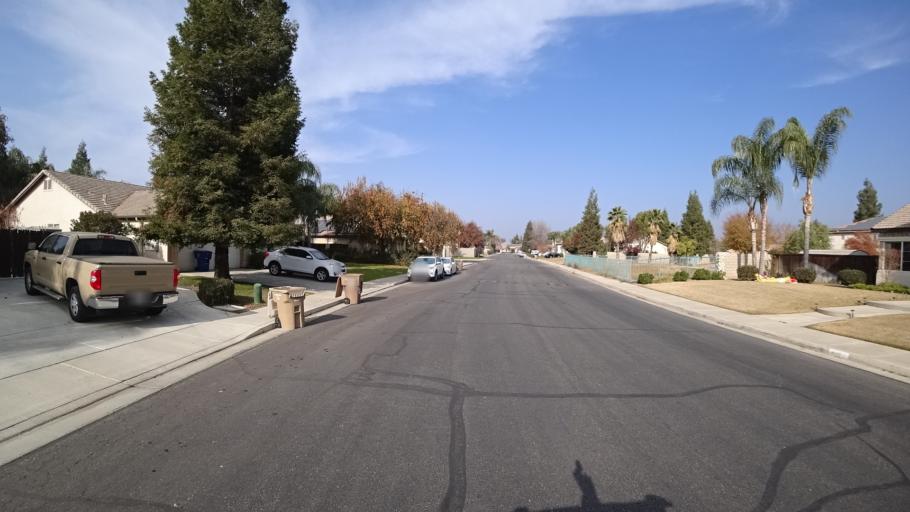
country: US
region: California
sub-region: Kern County
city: Greenacres
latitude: 35.4146
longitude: -119.1081
